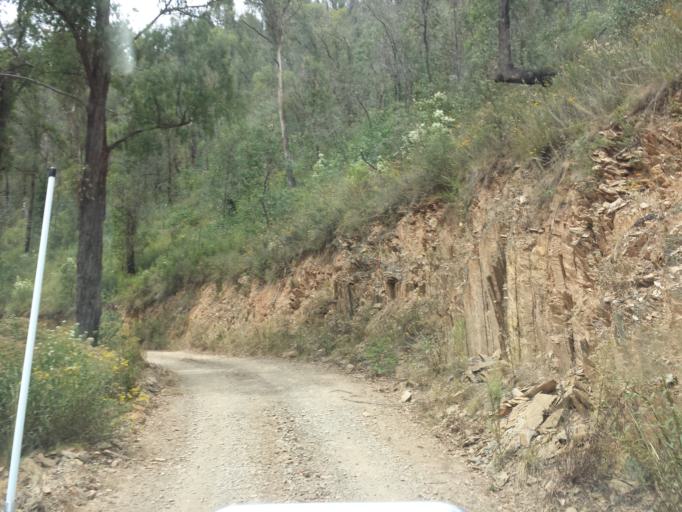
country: AU
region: Victoria
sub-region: Wellington
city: Heyfield
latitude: -37.7526
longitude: 146.4812
